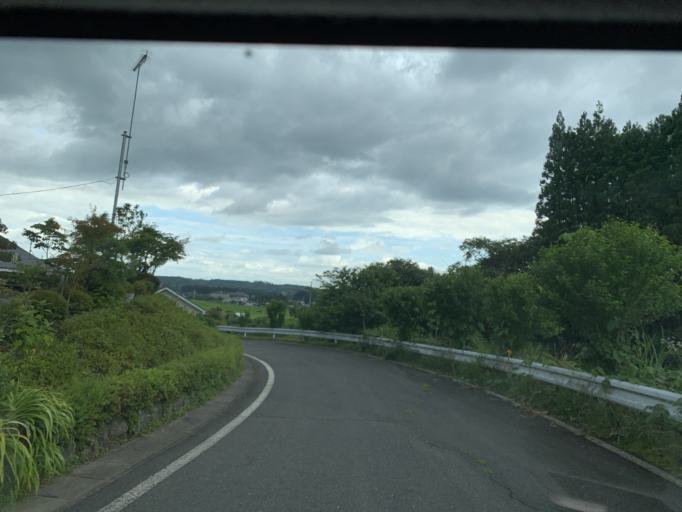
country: JP
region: Iwate
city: Ichinoseki
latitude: 38.9535
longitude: 141.0459
